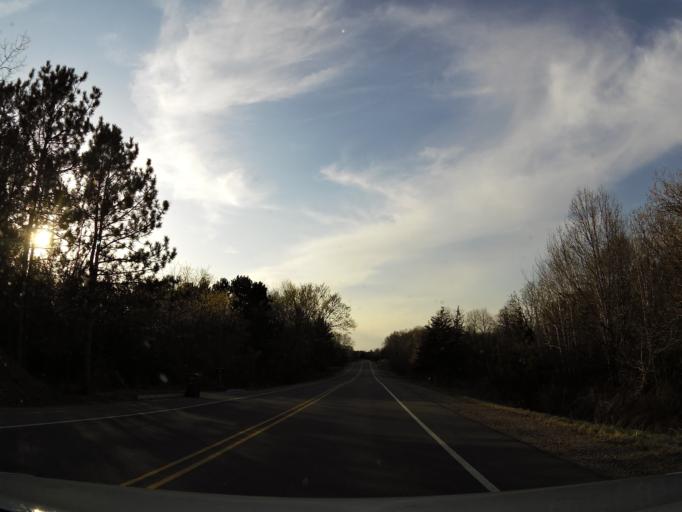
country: US
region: Minnesota
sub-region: Washington County
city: Lake Saint Croix Beach
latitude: 44.9208
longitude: -92.6892
